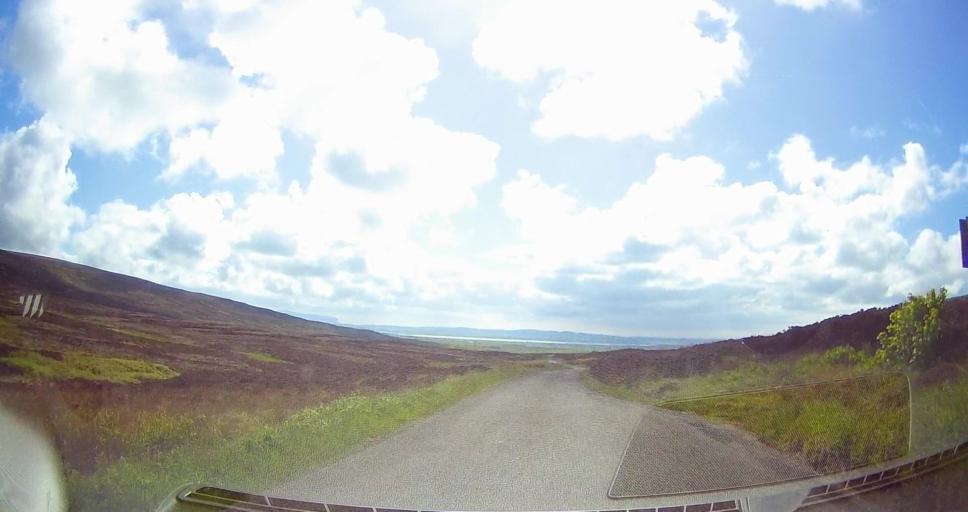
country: GB
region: Scotland
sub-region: Orkney Islands
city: Orkney
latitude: 59.0491
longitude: -3.1238
